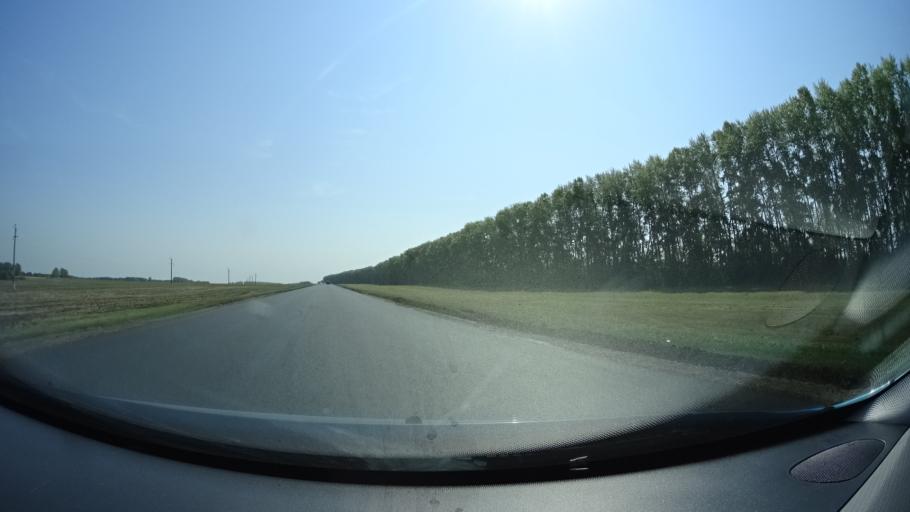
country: RU
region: Bashkortostan
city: Karmaskaly
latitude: 54.4075
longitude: 56.0745
